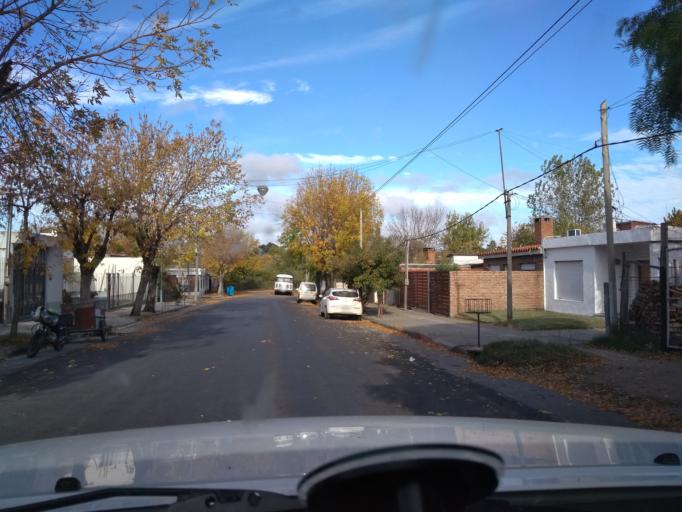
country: UY
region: Florida
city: Florida
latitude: -34.0968
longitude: -56.2229
